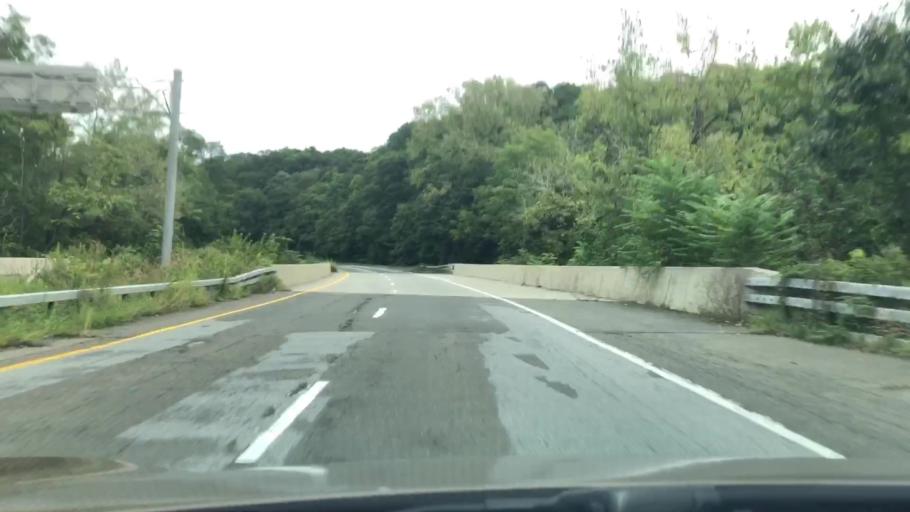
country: US
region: New York
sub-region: Westchester County
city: Sleepy Hollow
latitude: 41.1081
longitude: -73.8457
